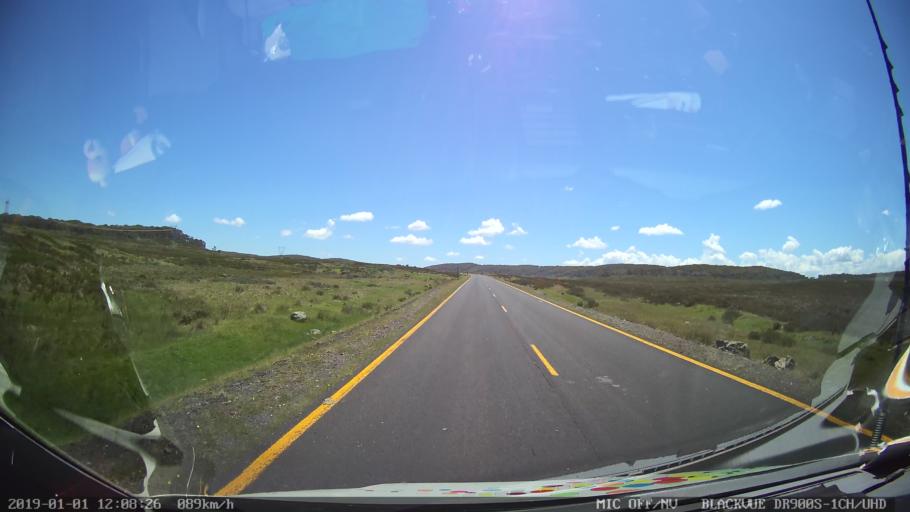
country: AU
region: New South Wales
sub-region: Tumut Shire
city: Tumut
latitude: -35.8204
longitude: 148.4947
